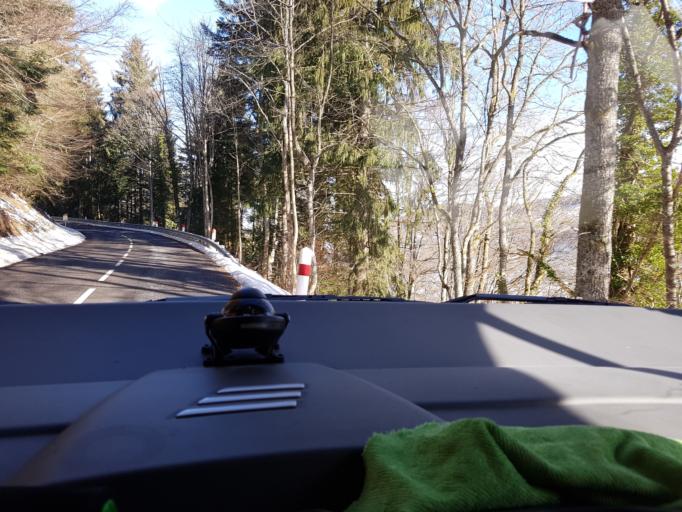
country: FR
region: Alsace
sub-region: Departement du Haut-Rhin
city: Metzeral
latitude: 47.9930
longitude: 7.0662
